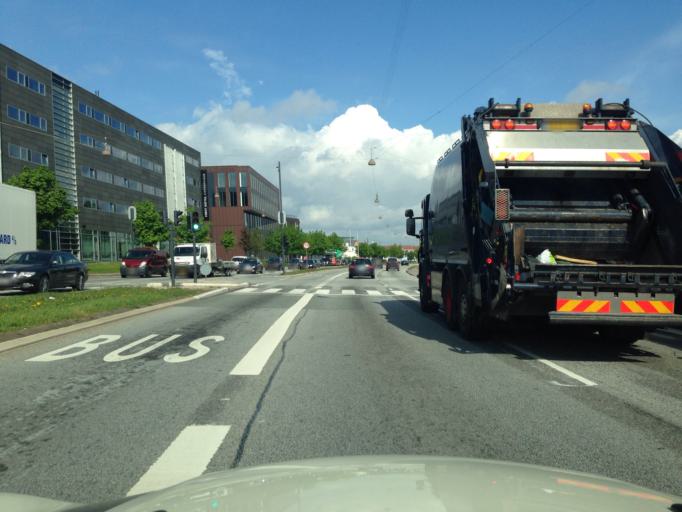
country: DK
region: Capital Region
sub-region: Frederiksberg Kommune
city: Frederiksberg
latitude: 55.6434
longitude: 12.5460
